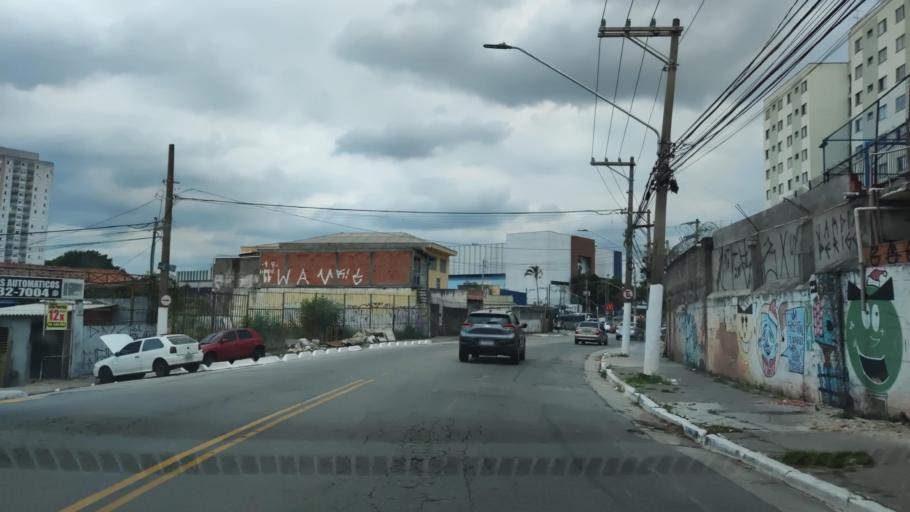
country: BR
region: Sao Paulo
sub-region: Sao Paulo
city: Sao Paulo
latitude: -23.4707
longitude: -46.6530
